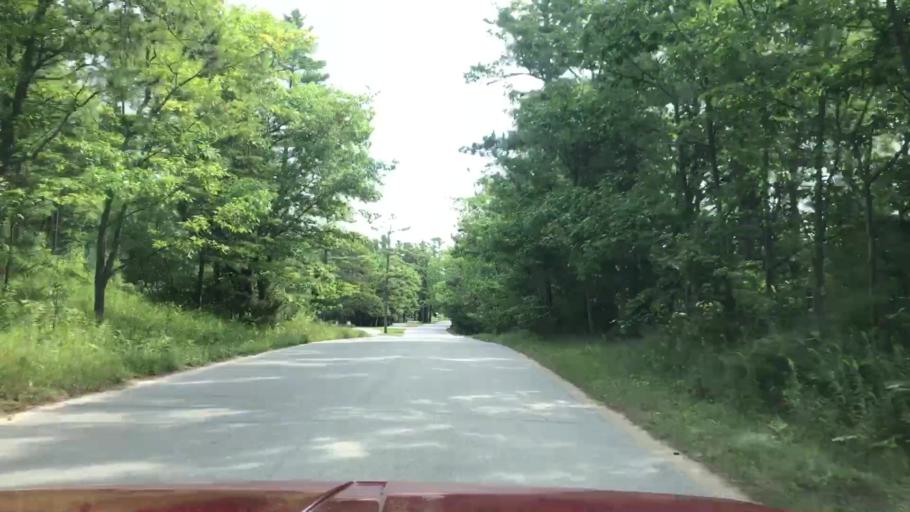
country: US
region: Michigan
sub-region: Charlevoix County
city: Charlevoix
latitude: 45.7468
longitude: -85.5263
